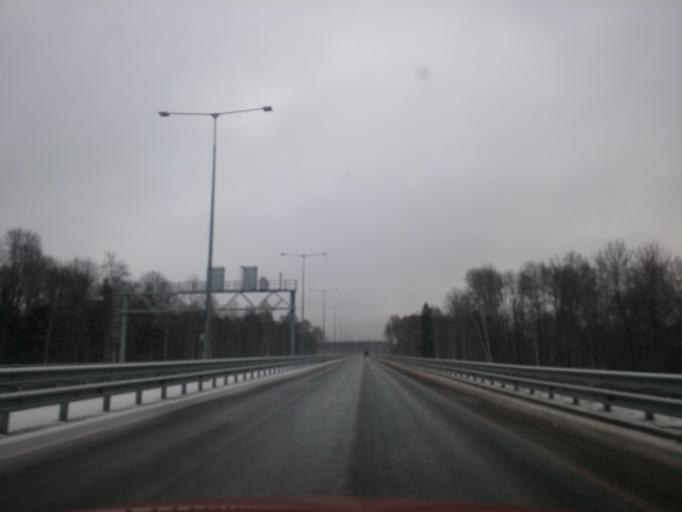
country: RU
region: Tverskaya
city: Likhoslavl'
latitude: 56.9638
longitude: 35.4744
